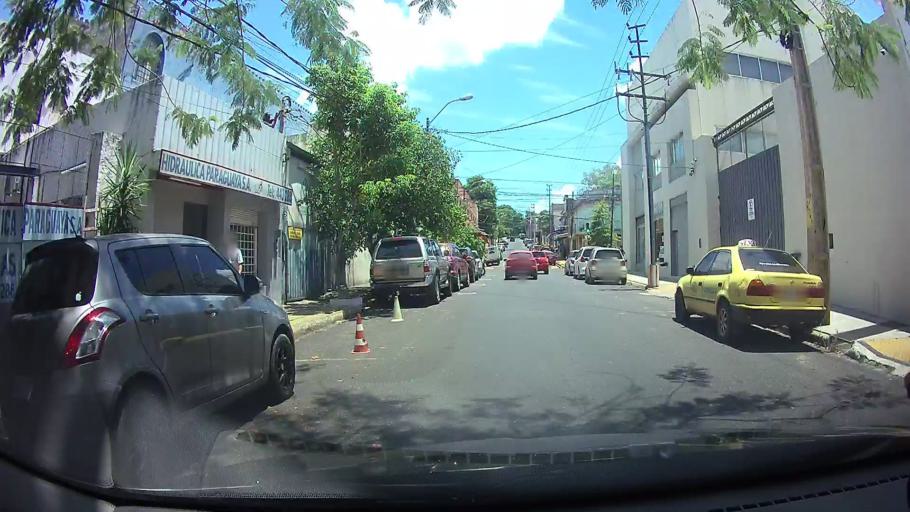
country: PY
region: Asuncion
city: Asuncion
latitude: -25.2913
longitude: -57.6321
